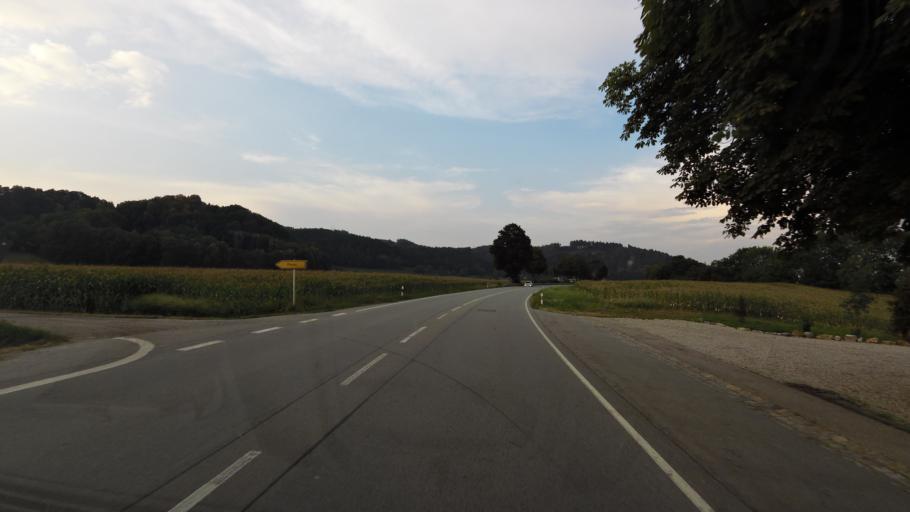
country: DE
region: Bavaria
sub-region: Lower Bavaria
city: Stubenberg
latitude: 48.2910
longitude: 13.0933
